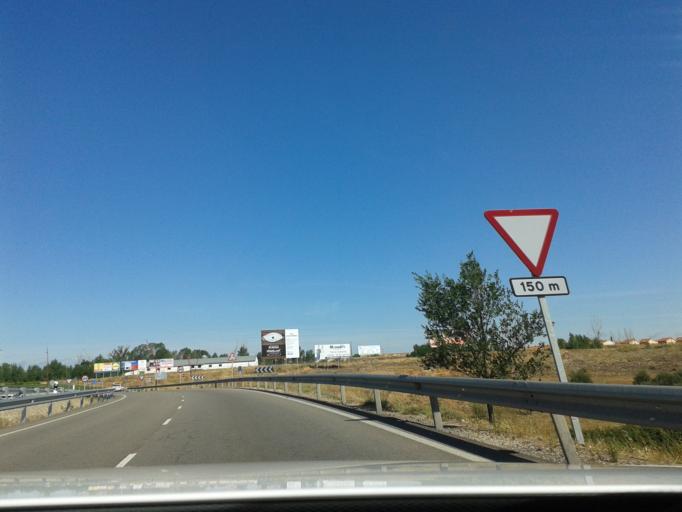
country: ES
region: Castille-La Mancha
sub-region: Provincia de Guadalajara
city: Azuqueca de Henares
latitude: 40.5739
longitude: -3.2521
